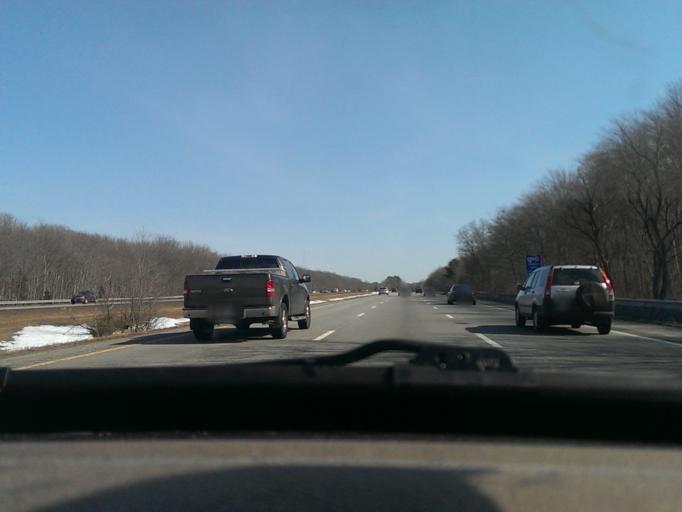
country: US
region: Massachusetts
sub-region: Bristol County
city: Seekonk
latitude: 41.7939
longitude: -71.3134
